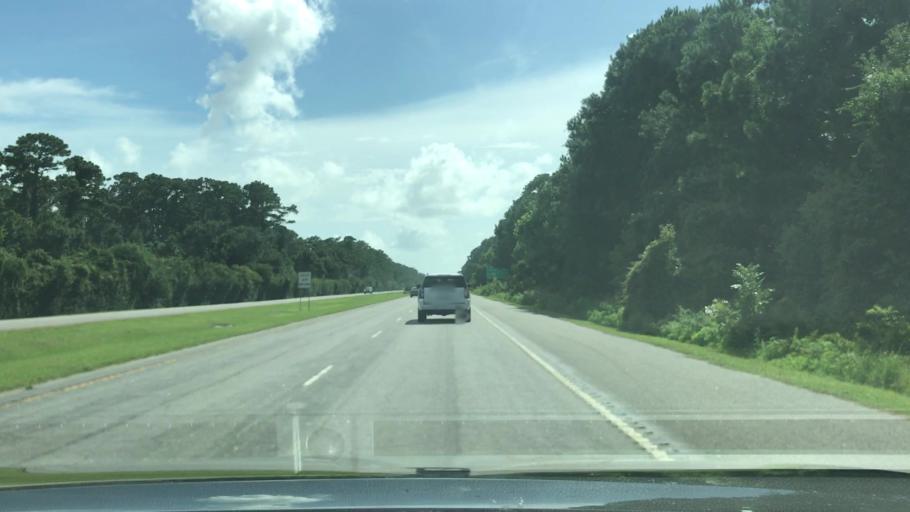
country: US
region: South Carolina
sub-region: Beaufort County
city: Hilton Head Island
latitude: 32.2059
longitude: -80.7454
